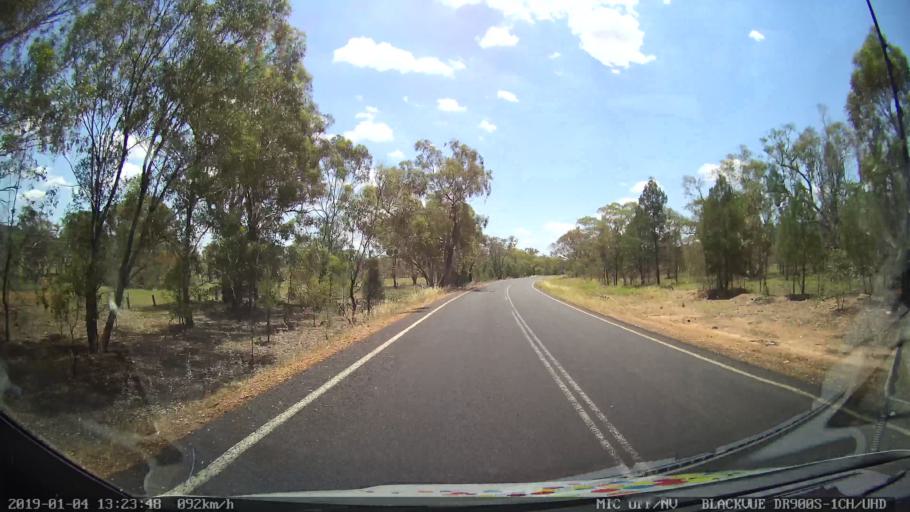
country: AU
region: New South Wales
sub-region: Parkes
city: Peak Hill
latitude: -32.7140
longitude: 148.5517
